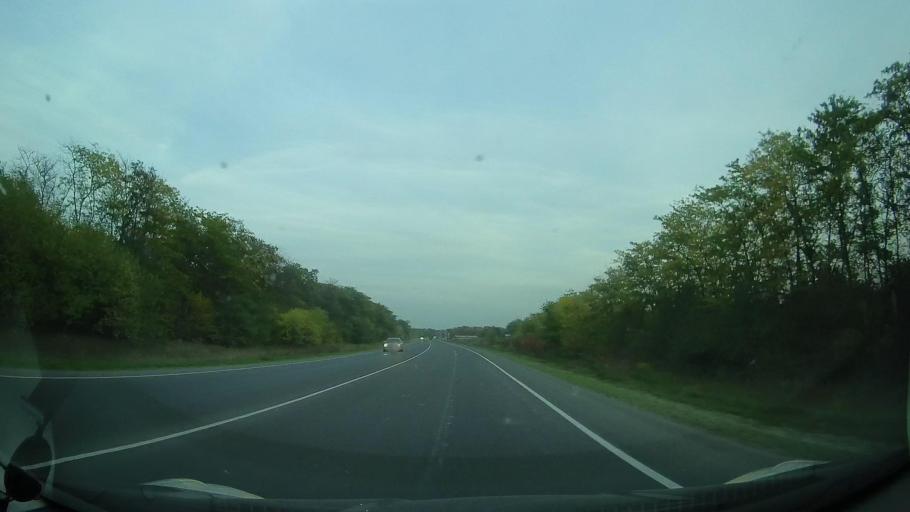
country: RU
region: Rostov
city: Kirovskaya
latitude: 46.9974
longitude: 39.9982
